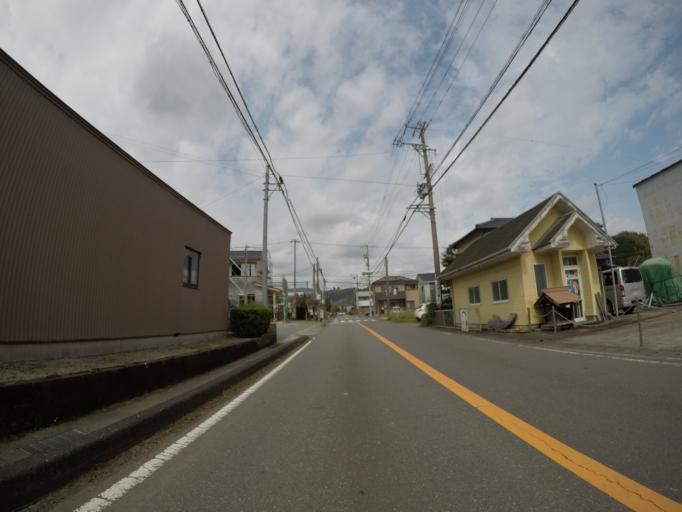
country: JP
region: Shizuoka
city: Shimada
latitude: 34.8539
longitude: 138.1819
